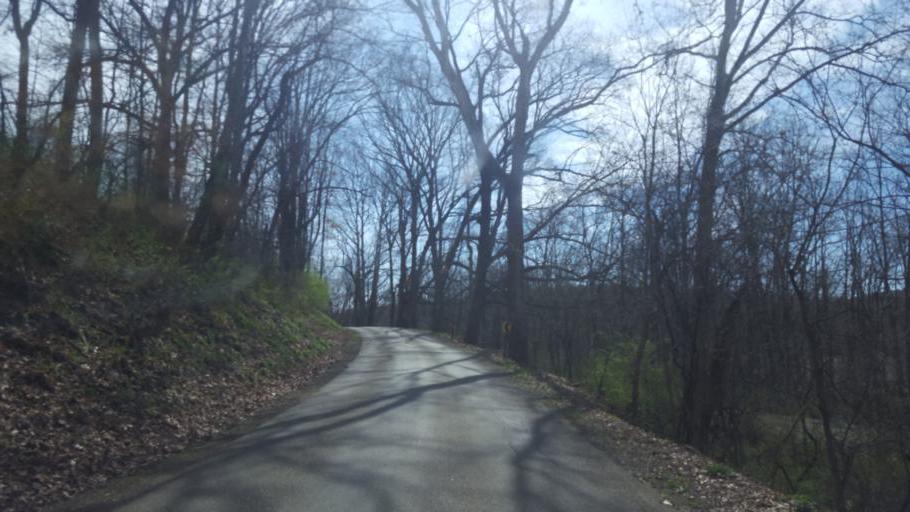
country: US
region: Ohio
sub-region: Knox County
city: Mount Vernon
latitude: 40.3762
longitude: -82.4588
